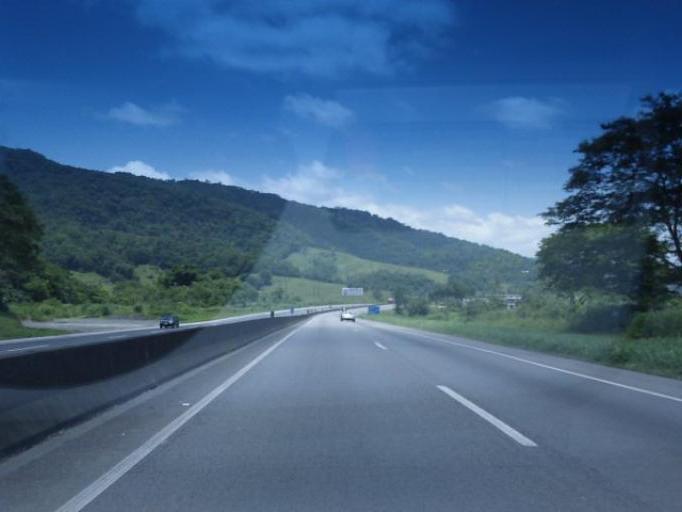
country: BR
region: Sao Paulo
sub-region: Miracatu
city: Miracatu
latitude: -24.3002
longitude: -47.4843
